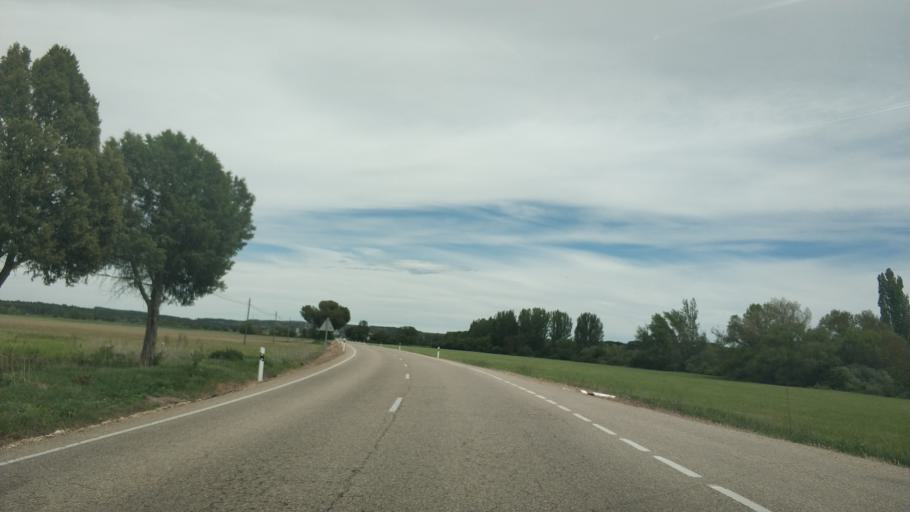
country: ES
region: Castille and Leon
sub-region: Provincia de Soria
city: Bayubas de Abajo
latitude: 41.5009
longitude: -2.8862
